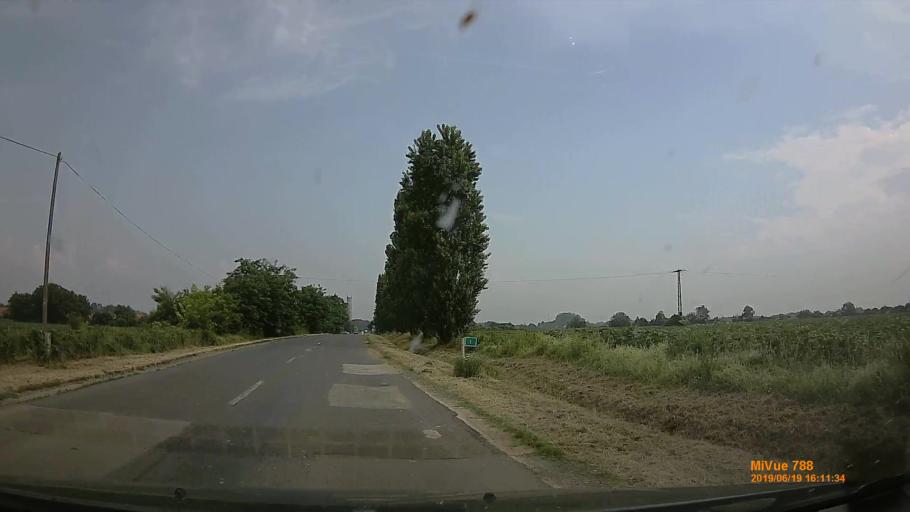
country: HU
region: Baranya
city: Szigetvar
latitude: 46.0564
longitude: 17.7792
